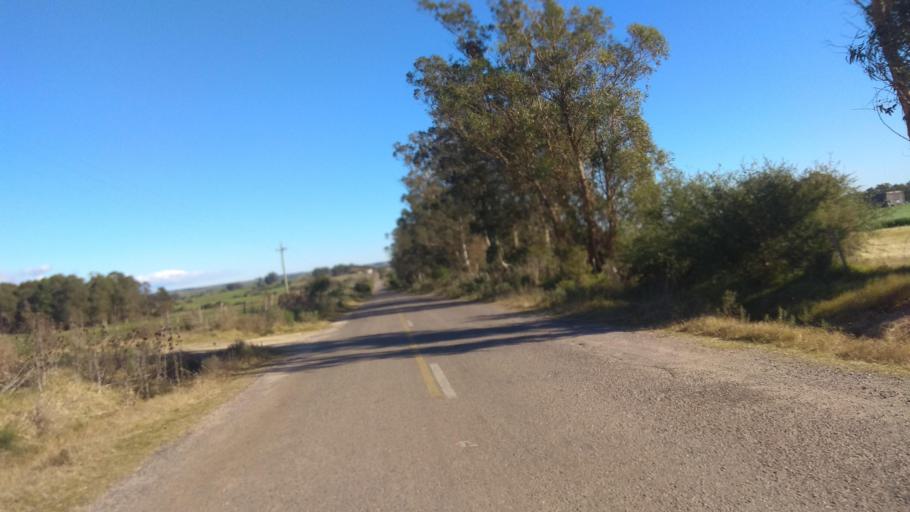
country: UY
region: Florida
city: Florida
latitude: -34.0497
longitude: -56.2558
